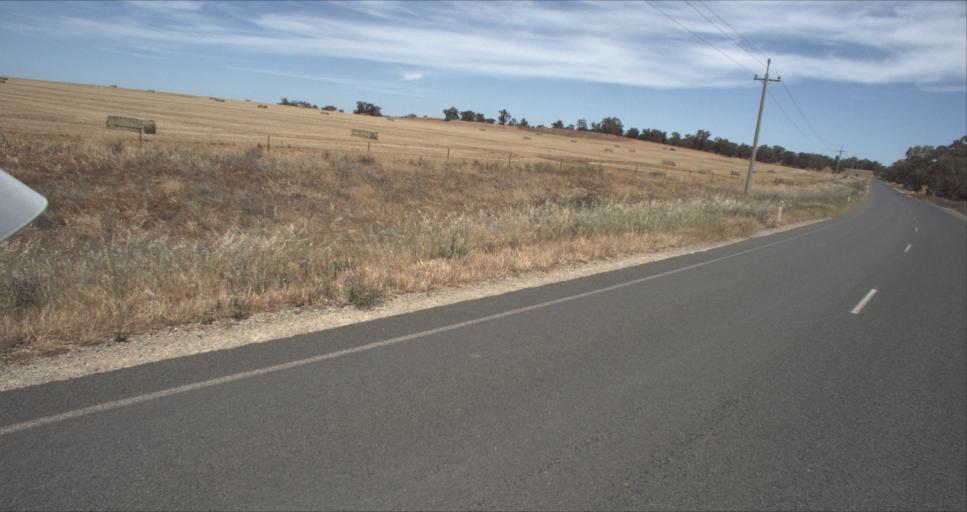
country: AU
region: New South Wales
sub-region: Leeton
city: Leeton
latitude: -34.6534
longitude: 146.4618
